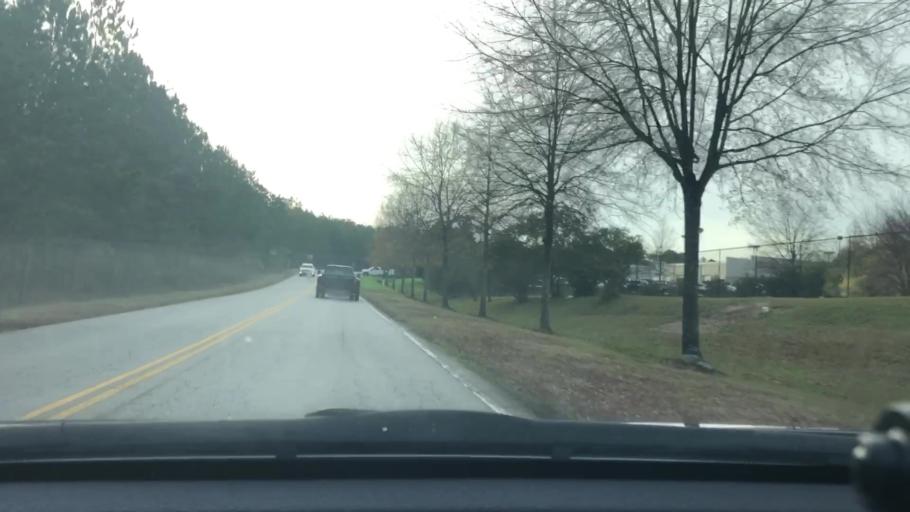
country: US
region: South Carolina
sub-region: Lexington County
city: Irmo
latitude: 34.0972
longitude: -81.1748
